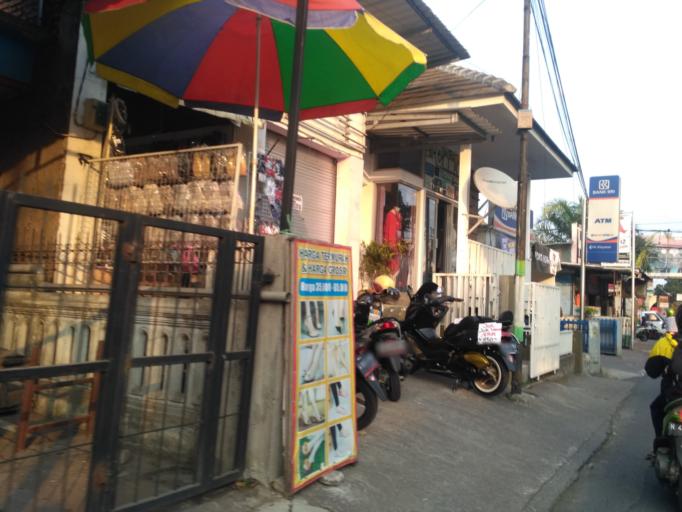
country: ID
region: East Java
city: Kepuh
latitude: -8.0063
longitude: 112.6186
